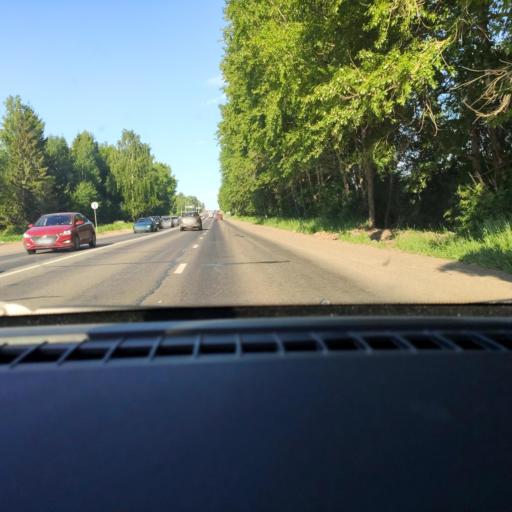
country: RU
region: Udmurtiya
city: Khokhryaki
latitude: 56.9109
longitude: 53.3729
